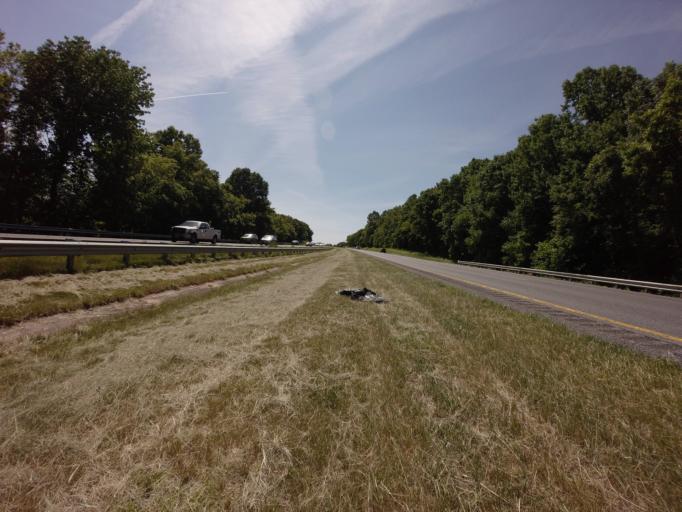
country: US
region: Maryland
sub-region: Frederick County
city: Urbana
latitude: 39.3408
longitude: -77.3844
